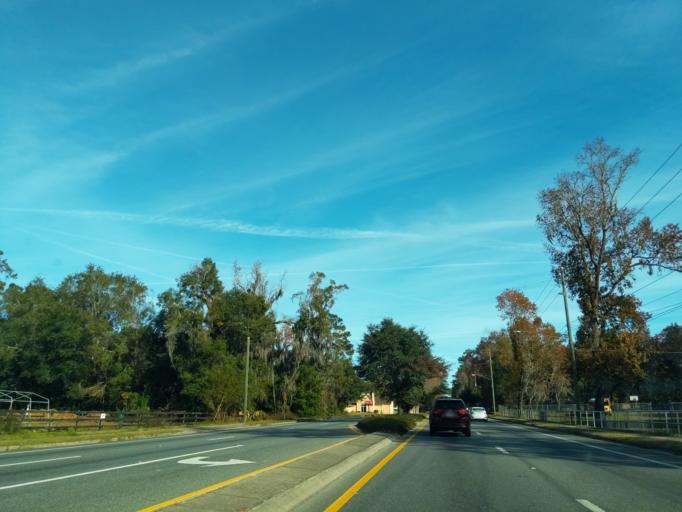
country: US
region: Florida
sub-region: Leon County
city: Tallahassee
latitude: 30.4126
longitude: -84.2765
